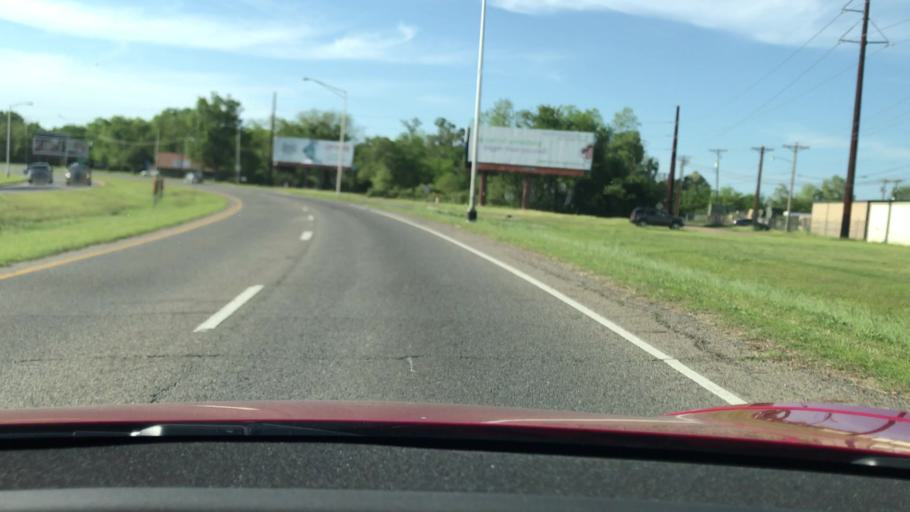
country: US
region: Louisiana
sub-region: Bossier Parish
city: Bossier City
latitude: 32.5018
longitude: -93.7249
